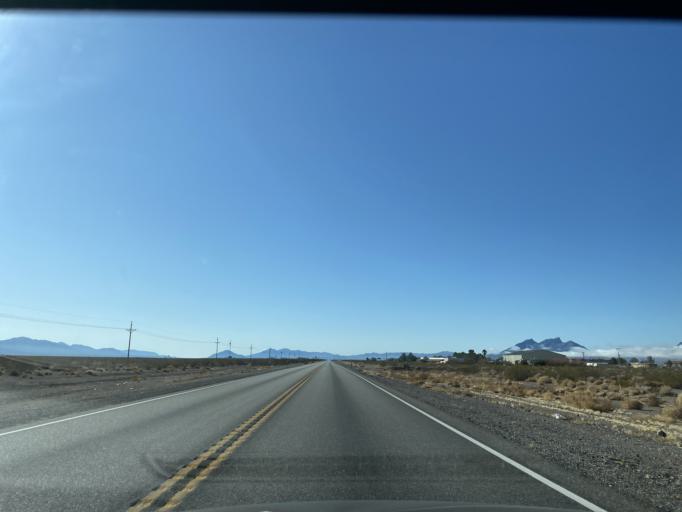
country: US
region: Nevada
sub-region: Nye County
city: Pahrump
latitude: 36.5001
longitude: -116.4214
